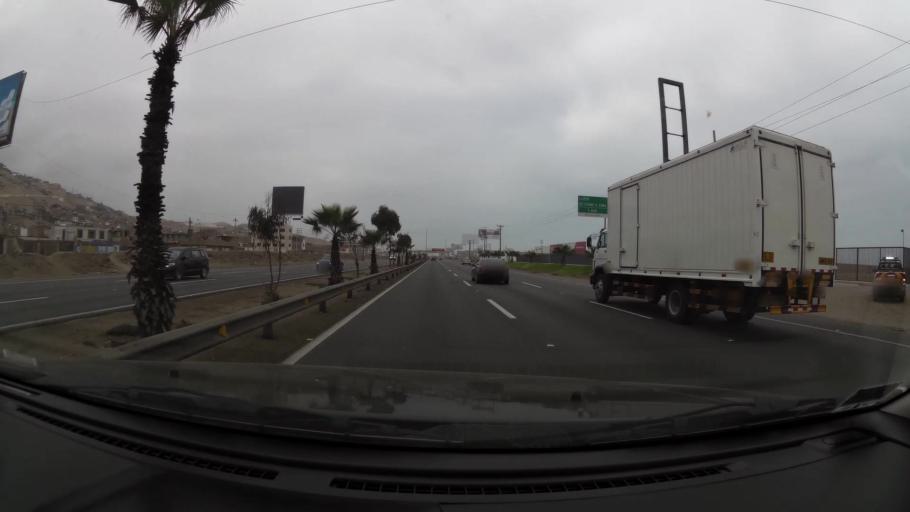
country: PE
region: Lima
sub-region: Lima
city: Surco
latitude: -12.2481
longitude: -76.9331
